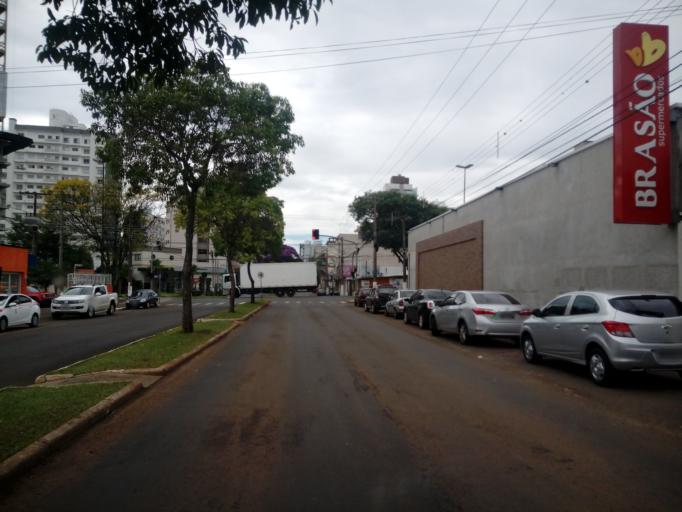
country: BR
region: Santa Catarina
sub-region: Chapeco
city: Chapeco
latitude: -27.1071
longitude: -52.6164
